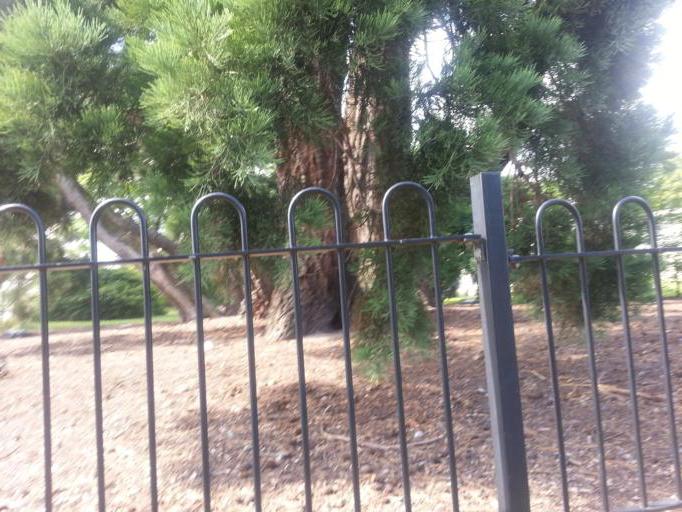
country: IE
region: Leinster
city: Glasnevin
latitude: 53.3723
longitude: -6.2702
